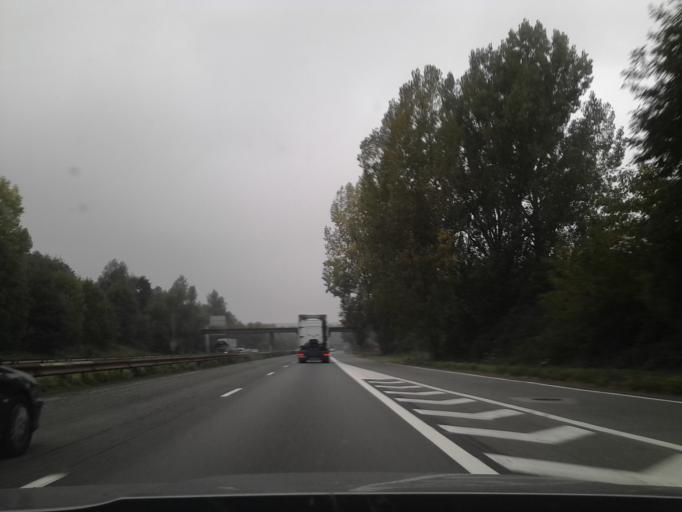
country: FR
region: Nord-Pas-de-Calais
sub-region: Departement du Nord
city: Saultain
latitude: 50.3460
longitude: 3.5724
